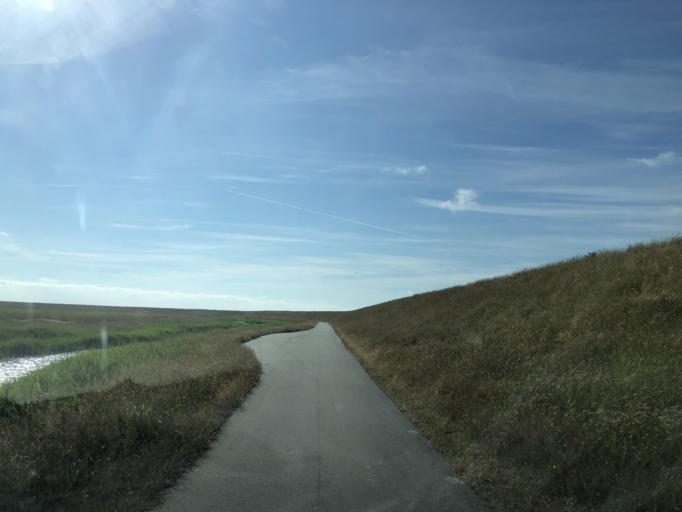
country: DK
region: South Denmark
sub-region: Esbjerg Kommune
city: Tjaereborg
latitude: 55.2931
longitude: 8.5652
